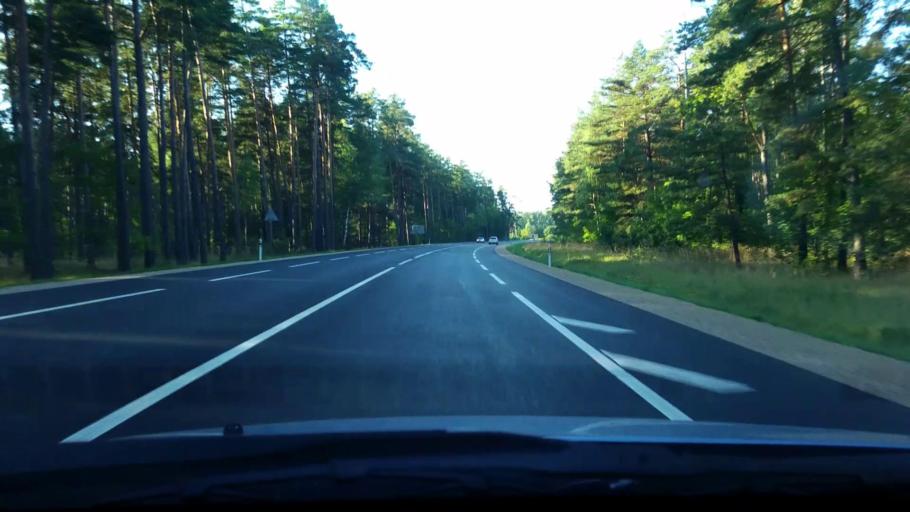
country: LV
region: Riga
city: Bergi
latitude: 57.0285
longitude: 24.3206
